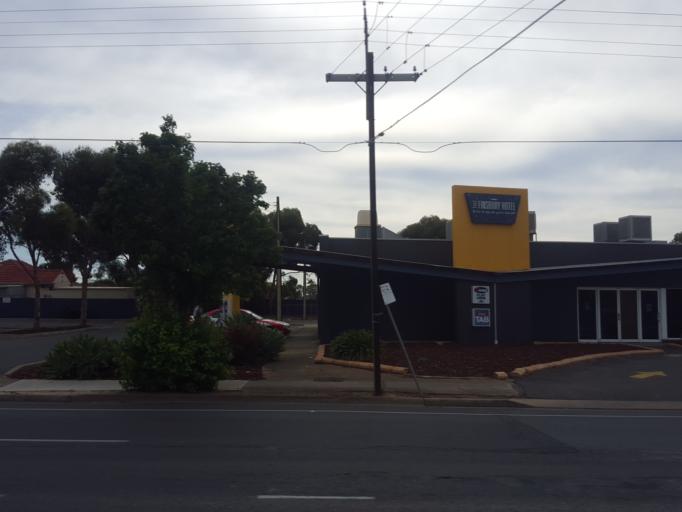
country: AU
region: South Australia
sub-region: Charles Sturt
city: Woodville North
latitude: -34.8696
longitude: 138.5480
